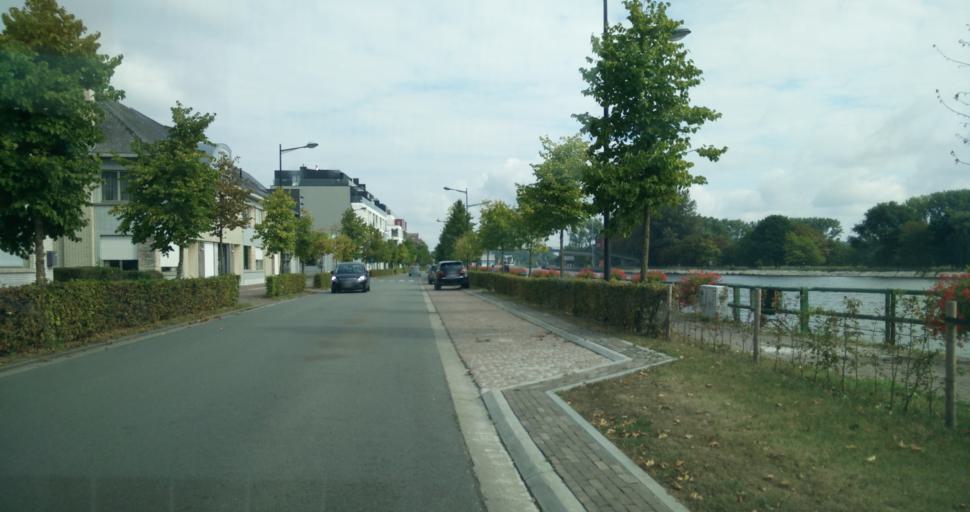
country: BE
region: Flanders
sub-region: Provincie Oost-Vlaanderen
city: Oudenaarde
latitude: 50.8446
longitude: 3.6108
